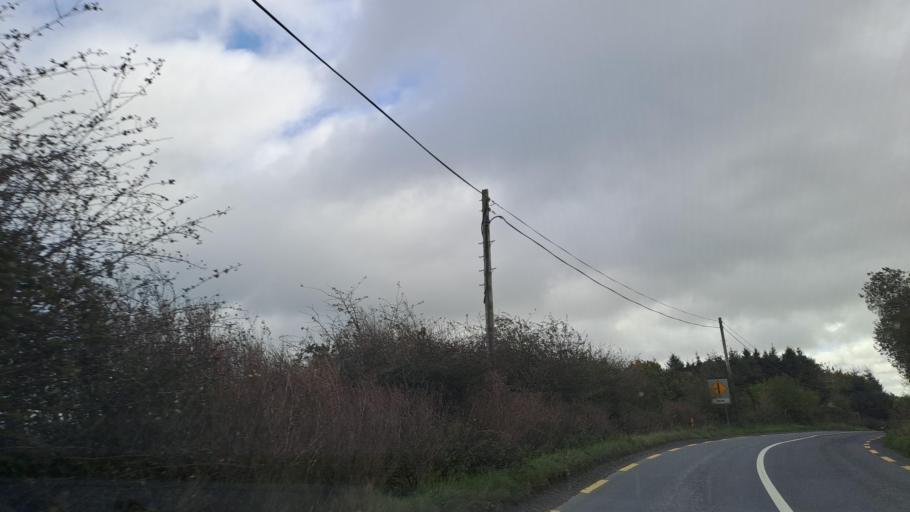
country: IE
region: Ulster
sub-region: An Cabhan
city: Kingscourt
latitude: 53.9301
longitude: -6.8817
